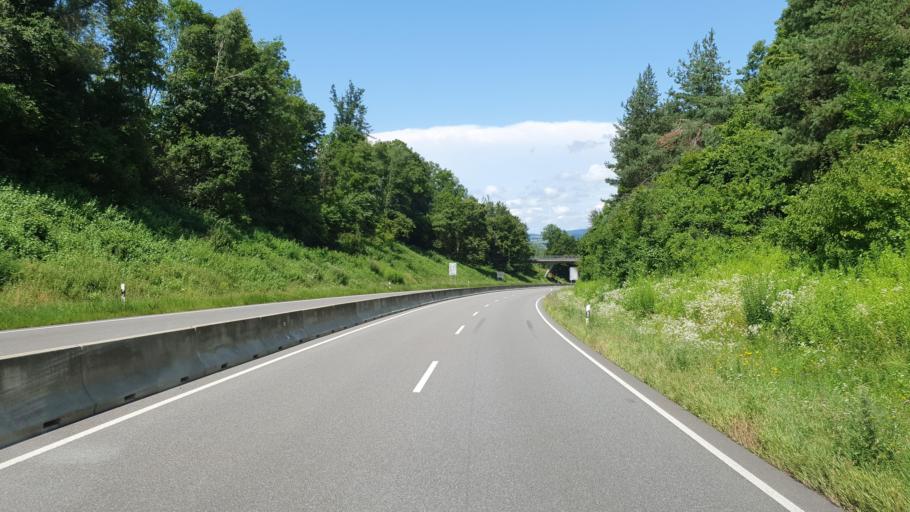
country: DE
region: Baden-Wuerttemberg
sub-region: Tuebingen Region
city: Uhldingen-Muhlhofen
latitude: 47.7215
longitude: 9.2398
